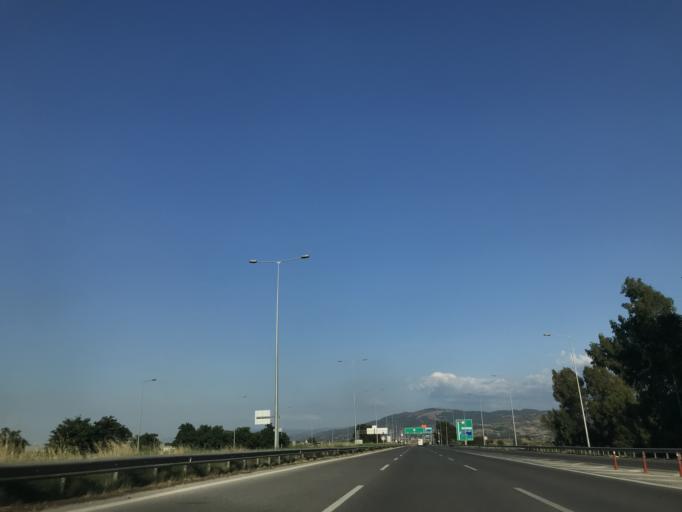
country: TR
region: Aydin
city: Aydin
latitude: 37.8187
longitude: 27.8476
